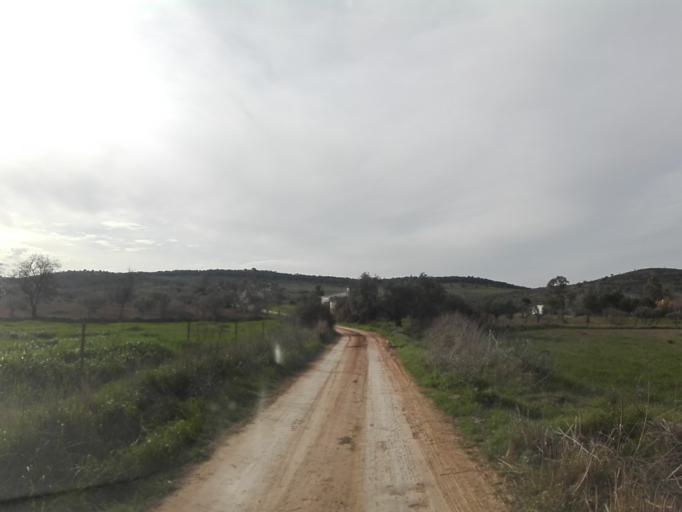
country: ES
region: Extremadura
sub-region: Provincia de Badajoz
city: Llerena
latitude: 38.2210
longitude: -6.0341
